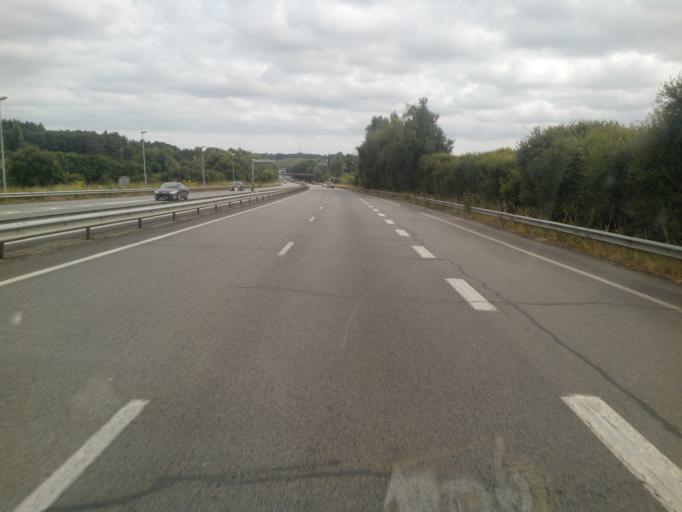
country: FR
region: Pays de la Loire
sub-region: Departement de la Loire-Atlantique
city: Treillieres
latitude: 47.3341
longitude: -1.6526
